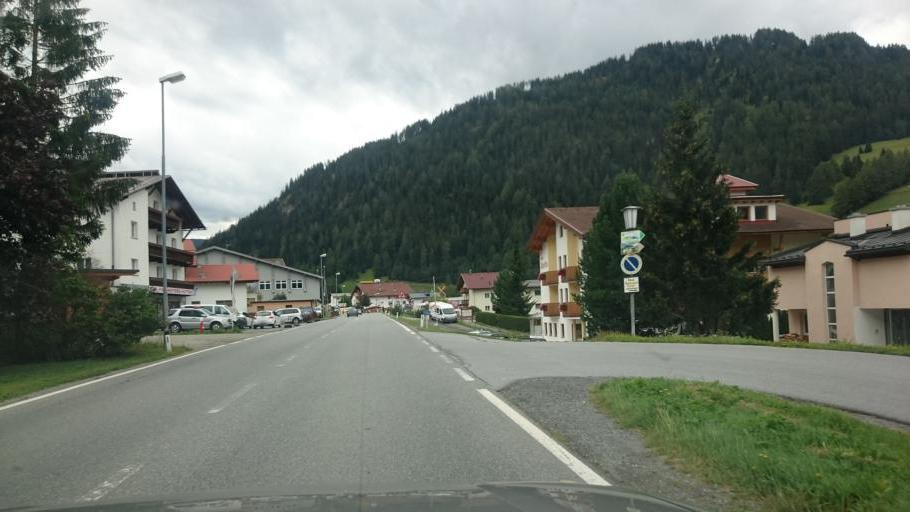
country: AT
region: Tyrol
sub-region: Politischer Bezirk Landeck
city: Nauders
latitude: 46.8936
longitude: 10.4986
